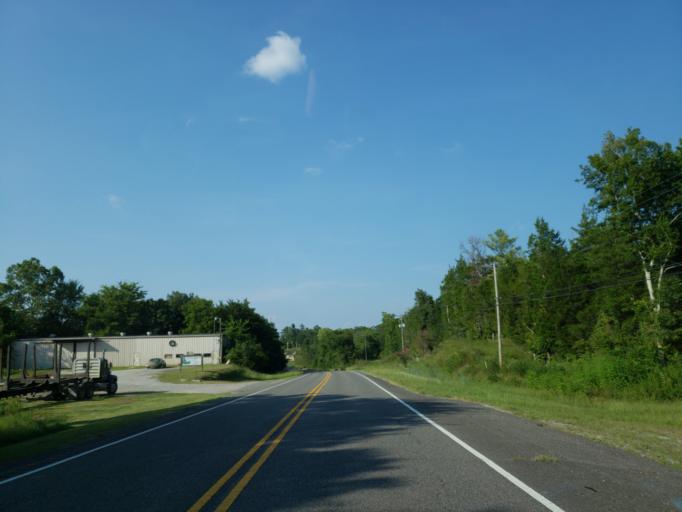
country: US
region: Alabama
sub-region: Sumter County
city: Livingston
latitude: 32.6380
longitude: -88.1729
